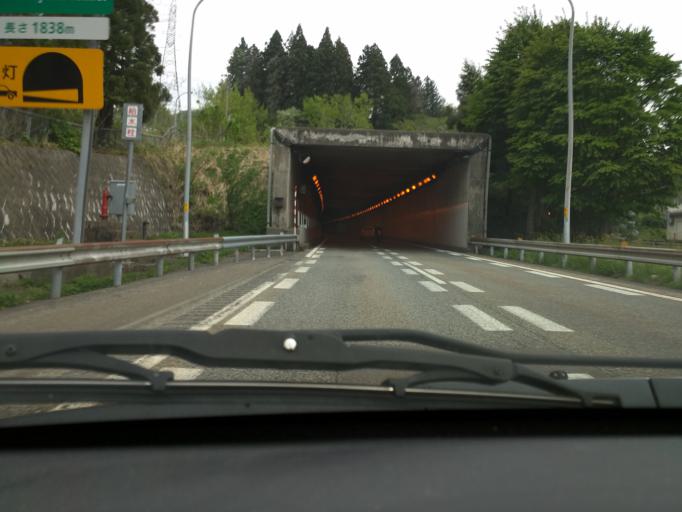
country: JP
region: Niigata
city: Ojiya
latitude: 37.2771
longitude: 138.7915
